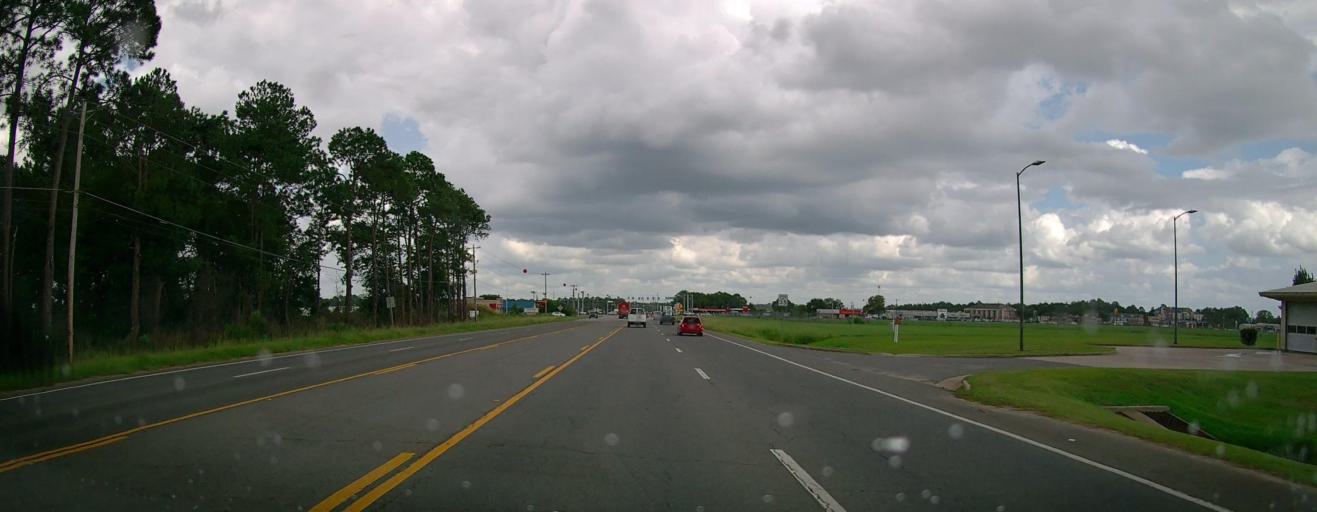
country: US
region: Georgia
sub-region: Coffee County
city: Douglas
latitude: 31.4879
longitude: -82.8554
